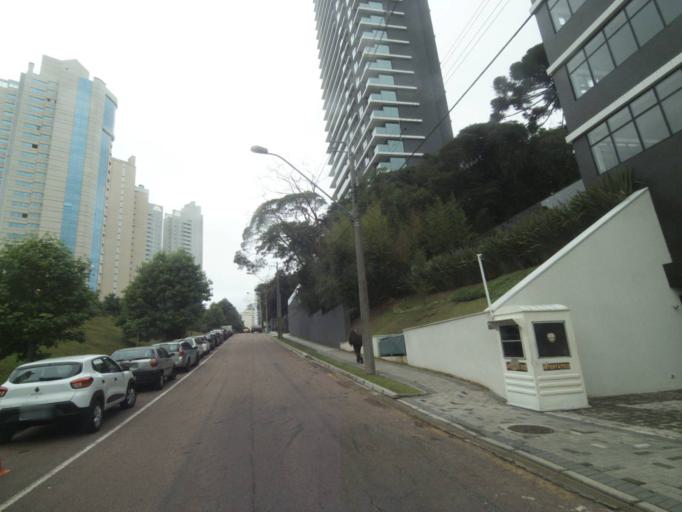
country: BR
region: Parana
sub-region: Curitiba
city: Curitiba
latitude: -25.4407
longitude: -49.3396
